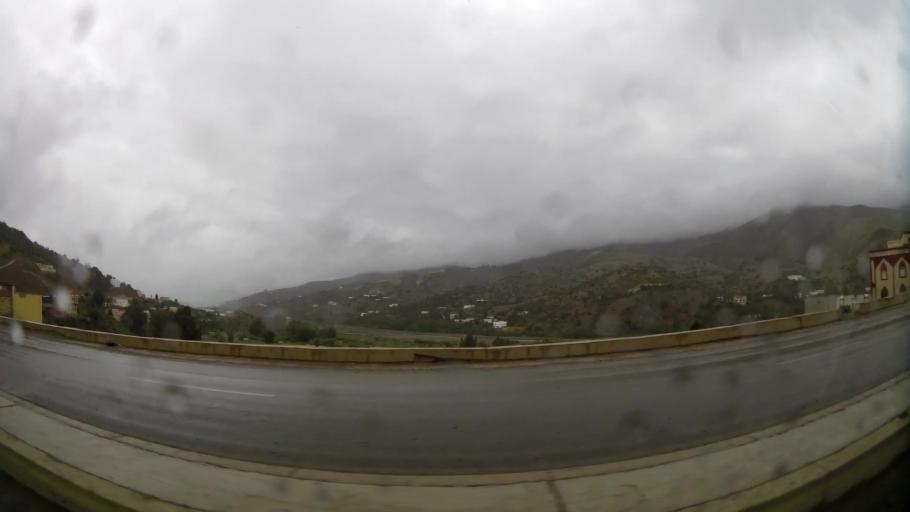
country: MA
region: Taza-Al Hoceima-Taounate
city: Imzourene
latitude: 35.0227
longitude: -3.8216
